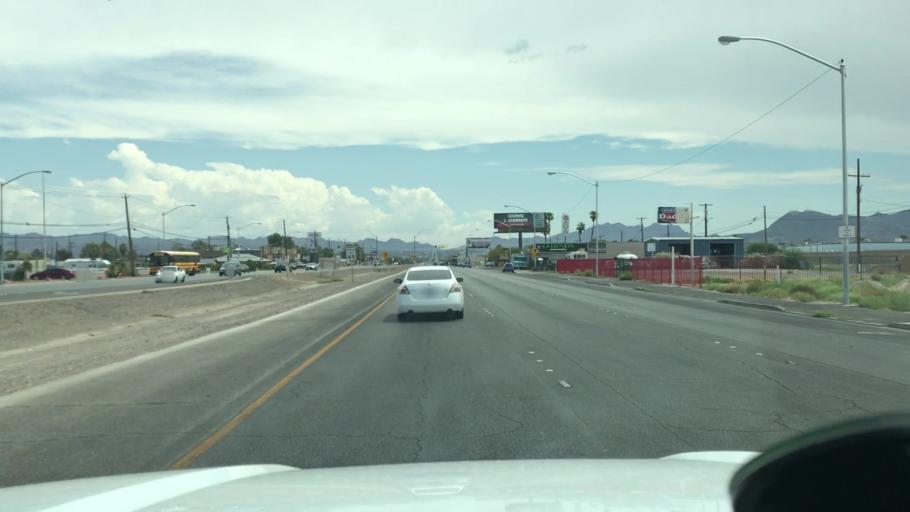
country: US
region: Nevada
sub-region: Clark County
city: Whitney
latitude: 36.0964
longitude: -115.0461
